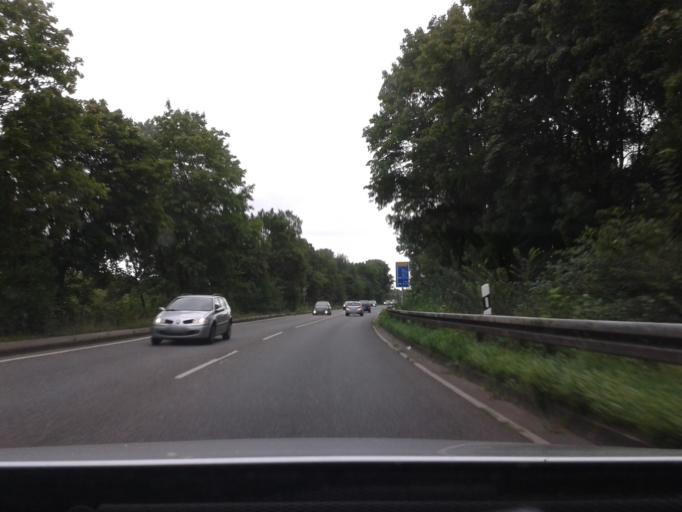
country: DE
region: North Rhine-Westphalia
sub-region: Regierungsbezirk Dusseldorf
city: Duisburg
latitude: 51.4382
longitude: 6.8097
